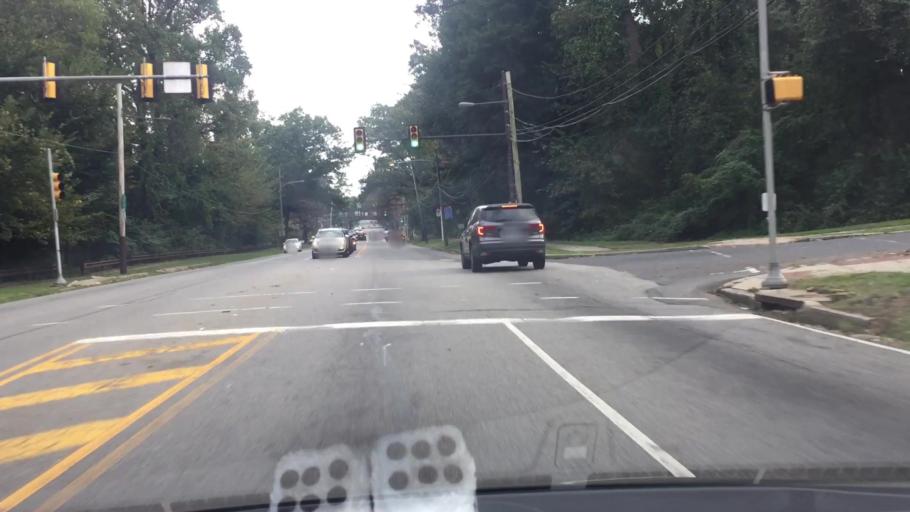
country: US
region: Pennsylvania
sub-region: Montgomery County
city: Bala-Cynwyd
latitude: 39.9879
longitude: -75.2163
